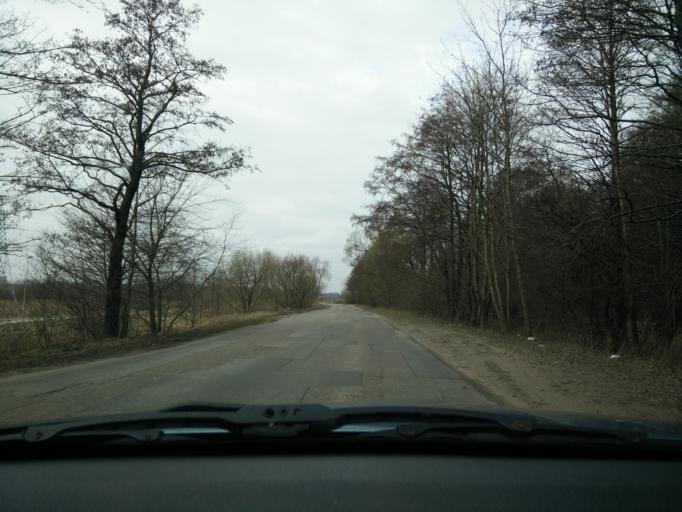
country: LT
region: Klaipedos apskritis
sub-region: Klaipeda
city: Klaipeda
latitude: 55.7230
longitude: 21.1693
